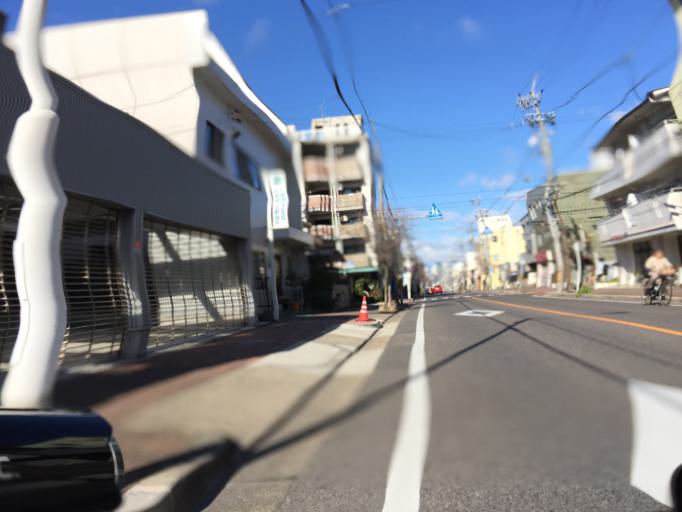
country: JP
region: Aichi
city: Nagoya-shi
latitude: 35.1617
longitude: 136.9429
